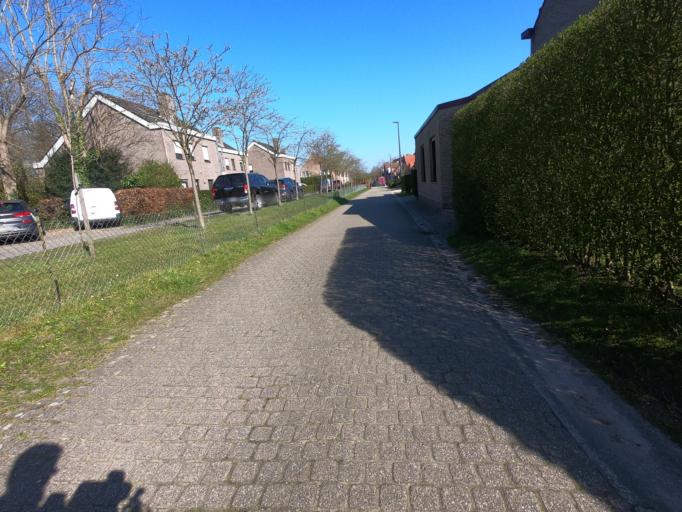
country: BE
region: Flanders
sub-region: Provincie Oost-Vlaanderen
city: De Pinte
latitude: 50.9973
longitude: 3.6499
